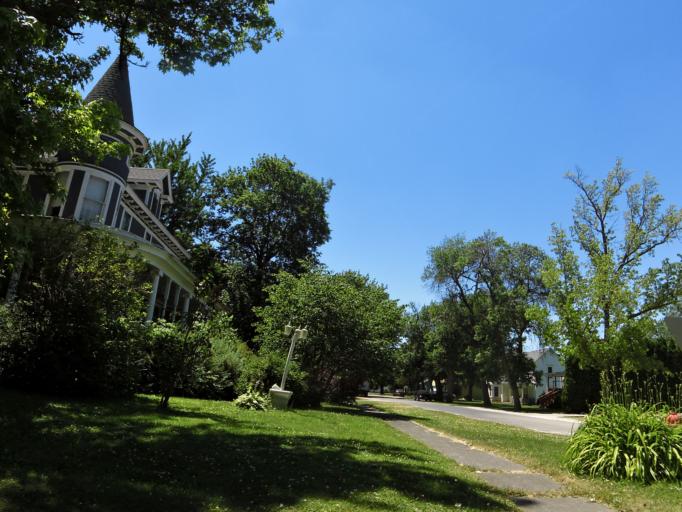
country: US
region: Illinois
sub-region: Livingston County
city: Chatsworth
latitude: 40.7570
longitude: -88.1919
